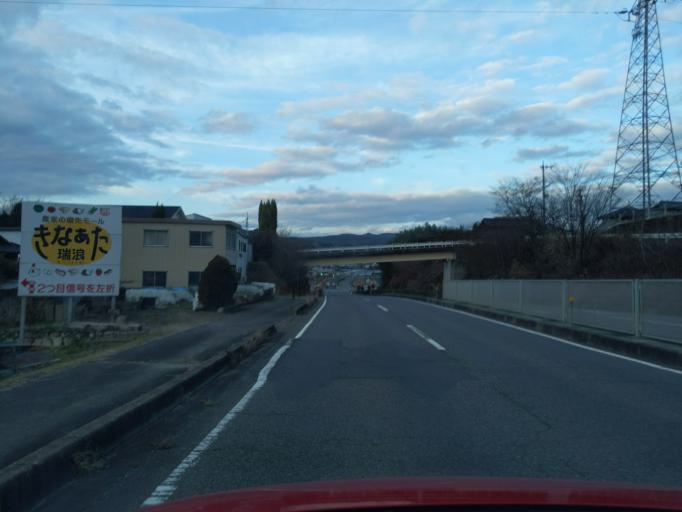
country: JP
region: Gifu
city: Mizunami
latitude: 35.3759
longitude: 137.2667
